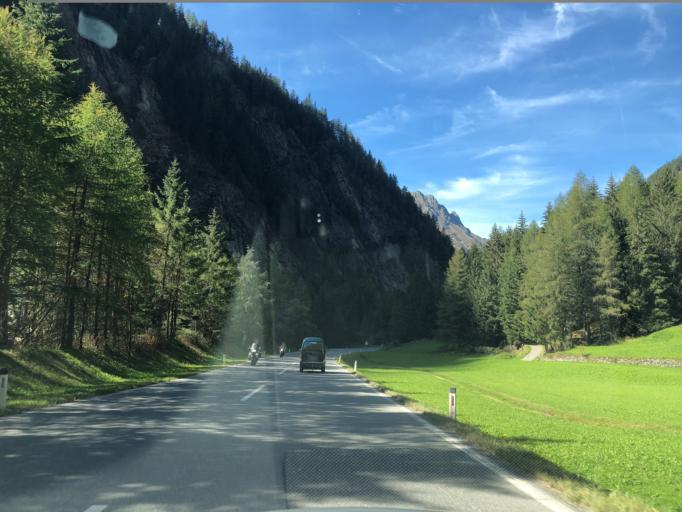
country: AT
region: Tyrol
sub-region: Politischer Bezirk Imst
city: Soelden
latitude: 47.0342
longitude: 10.9890
